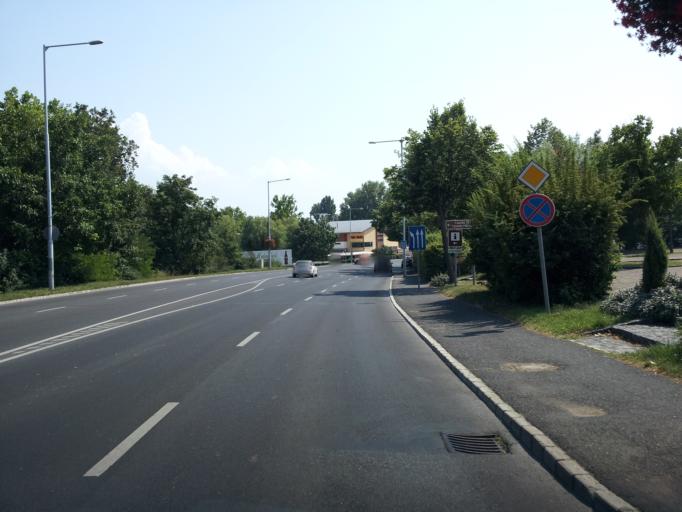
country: HU
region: Veszprem
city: Balatonfured
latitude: 46.9533
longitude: 17.8886
